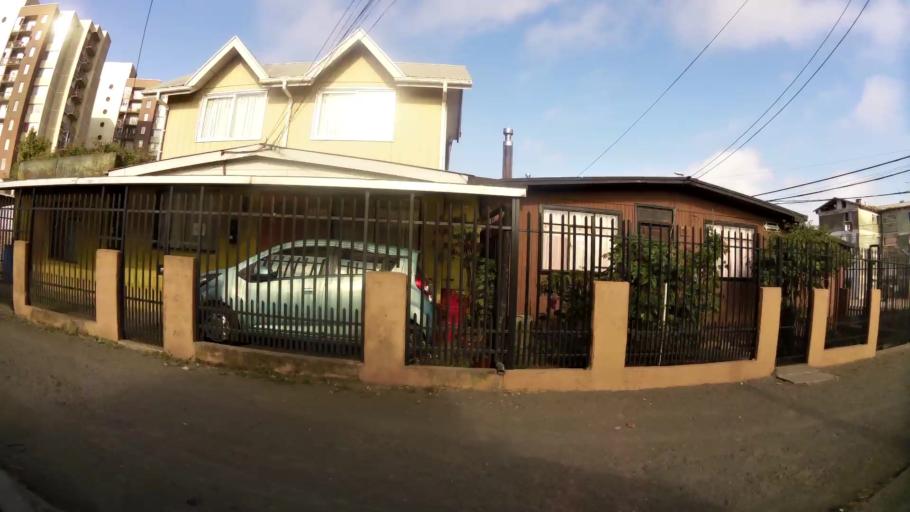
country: CL
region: Biobio
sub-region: Provincia de Concepcion
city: Concepcion
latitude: -36.7892
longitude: -73.0910
